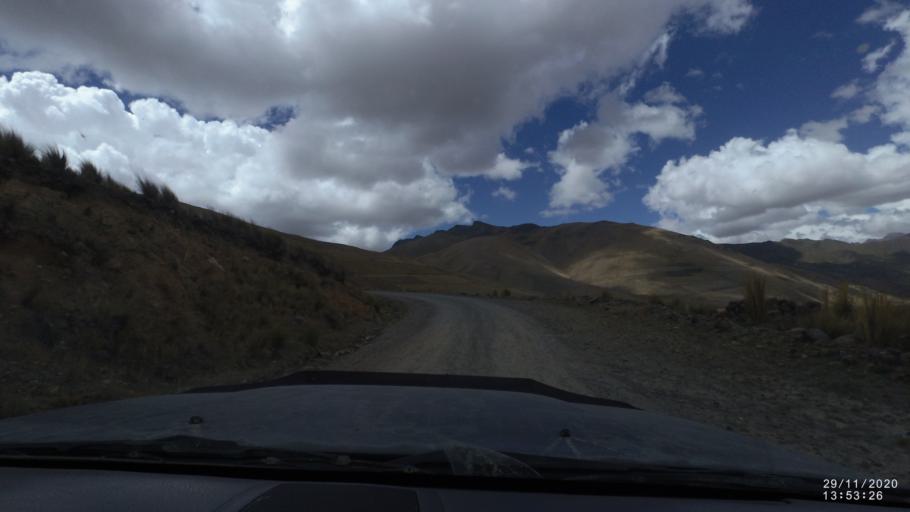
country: BO
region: Cochabamba
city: Sipe Sipe
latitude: -17.1739
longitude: -66.3532
